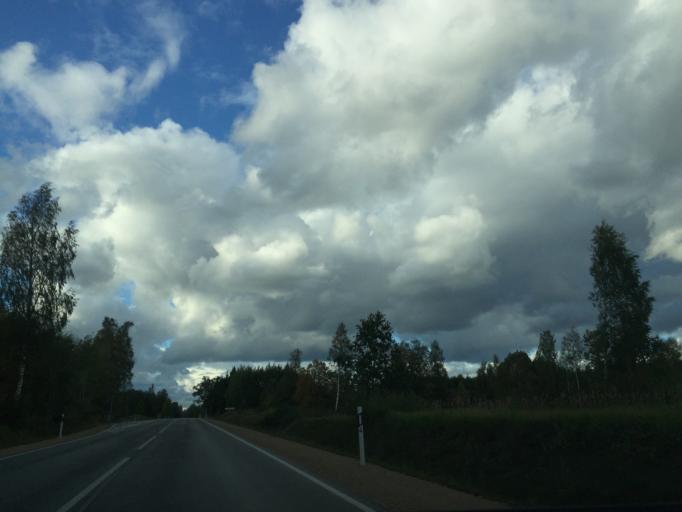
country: LV
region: Ligatne
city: Ligatne
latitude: 57.1708
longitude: 25.0443
